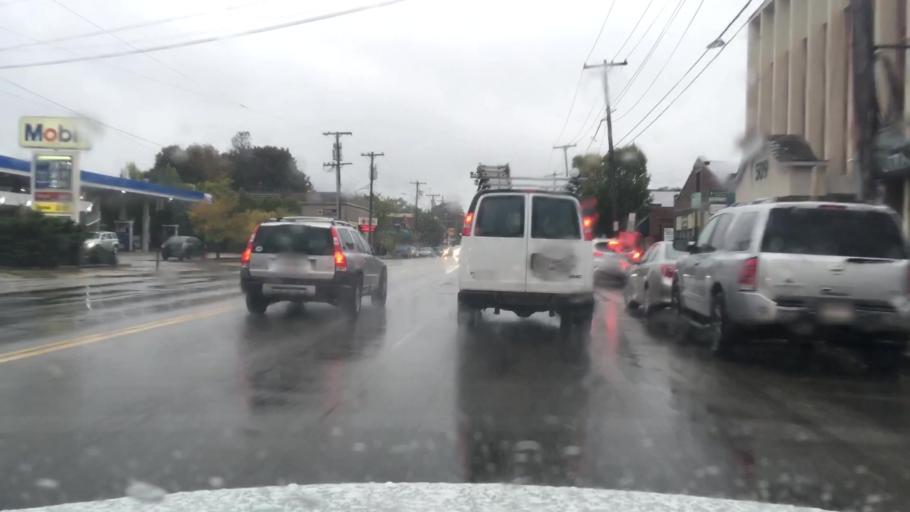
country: US
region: Maine
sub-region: Cumberland County
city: Portland
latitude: 43.6674
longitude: -70.2787
